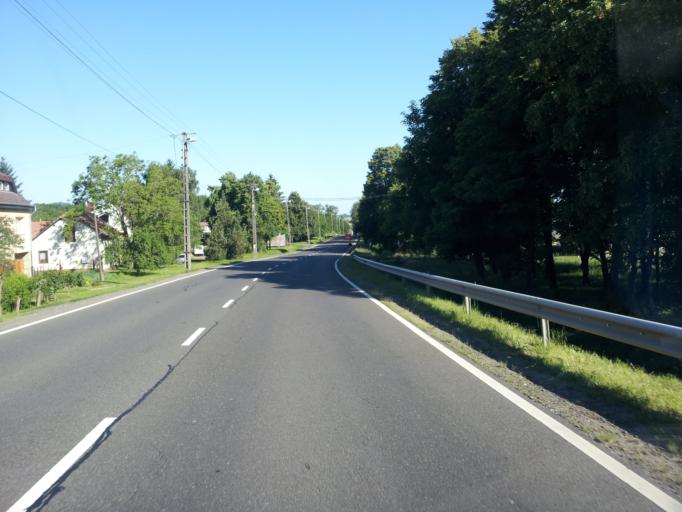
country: HU
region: Nograd
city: Nagyoroszi
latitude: 47.9961
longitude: 19.0981
